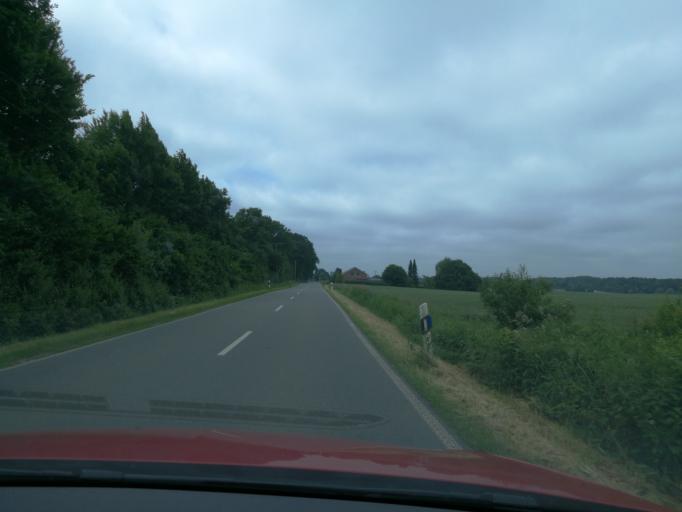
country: DE
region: Schleswig-Holstein
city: Politz
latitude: 53.7599
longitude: 10.3852
